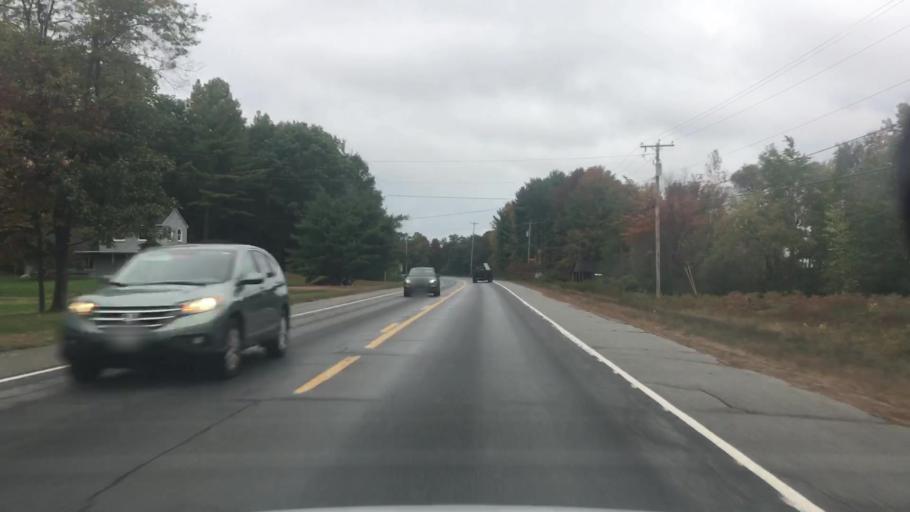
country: US
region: Maine
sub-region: Kennebec County
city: Belgrade
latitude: 44.4389
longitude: -69.8321
